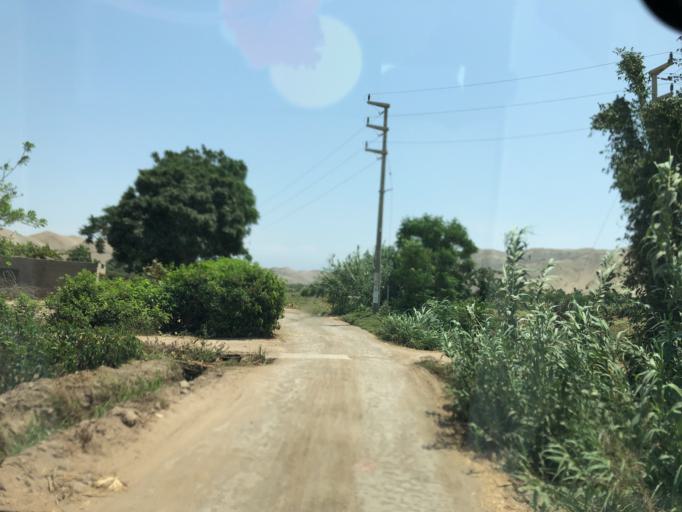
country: PE
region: Lima
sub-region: Provincia de Canete
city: Quilmana
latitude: -13.0033
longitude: -76.4501
